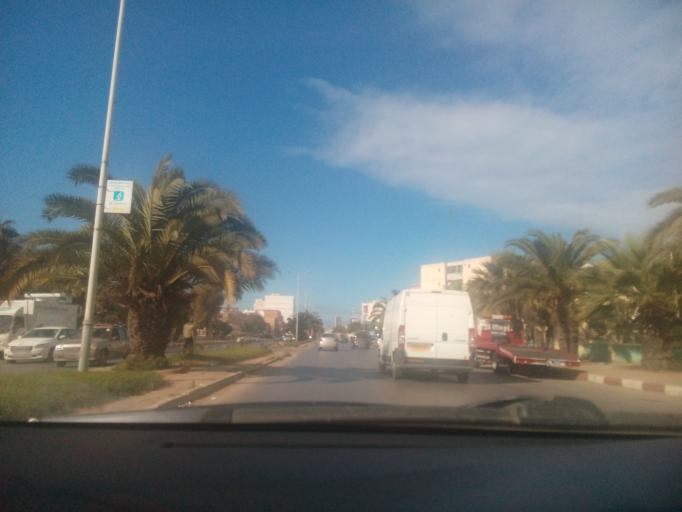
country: DZ
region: Oran
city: Oran
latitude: 35.6848
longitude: -0.6115
